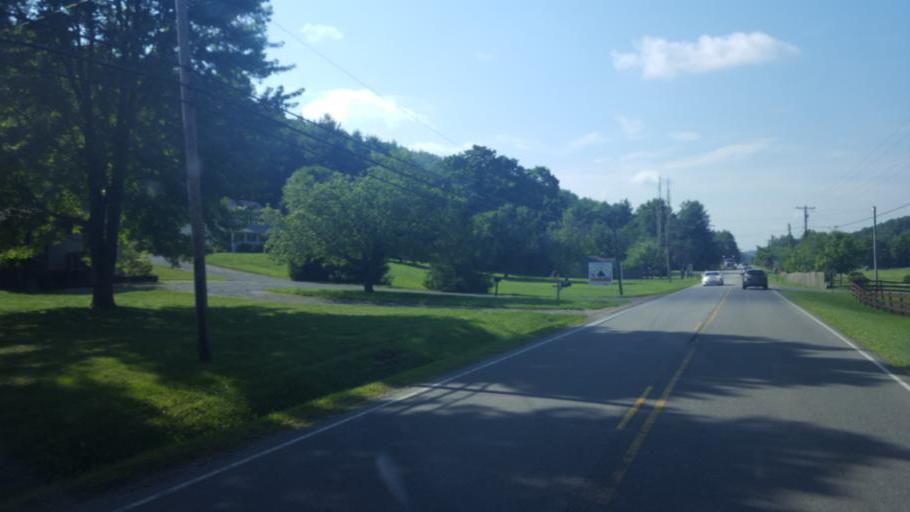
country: US
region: North Carolina
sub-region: Avery County
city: Newland
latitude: 36.1208
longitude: -81.9337
